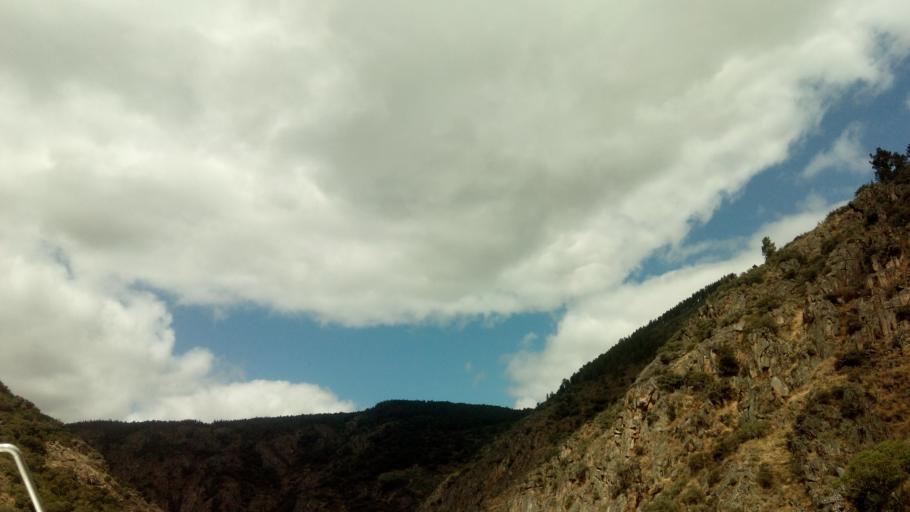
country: ES
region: Galicia
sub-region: Provincia de Lugo
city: Lobios
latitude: 42.4000
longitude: -7.5634
